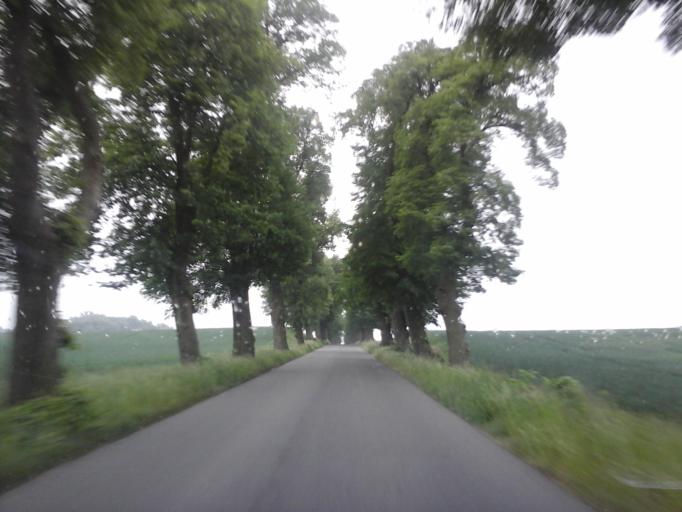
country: PL
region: West Pomeranian Voivodeship
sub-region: Powiat choszczenski
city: Pelczyce
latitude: 53.0915
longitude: 15.3507
